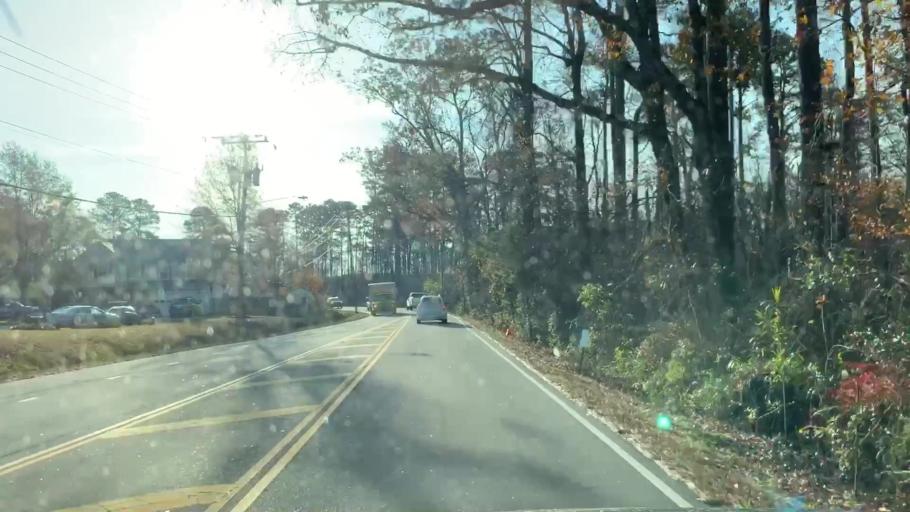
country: US
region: Virginia
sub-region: City of Chesapeake
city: Chesapeake
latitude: 36.7630
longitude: -76.1482
